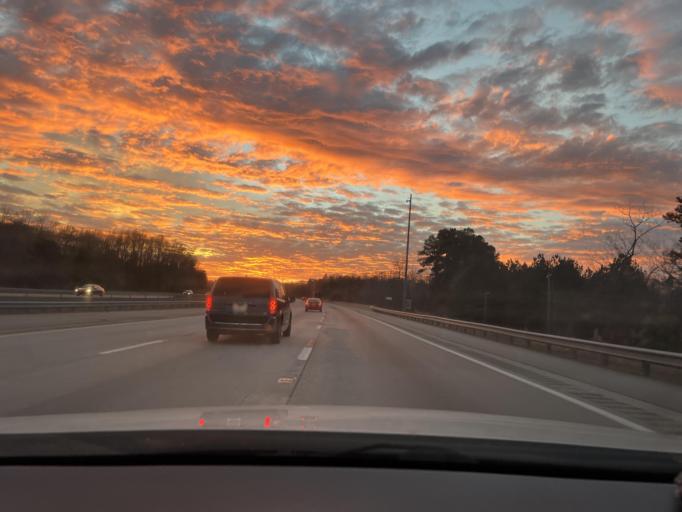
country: US
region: North Carolina
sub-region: Guilford County
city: Forest Oaks
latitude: 36.0306
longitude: -79.7180
